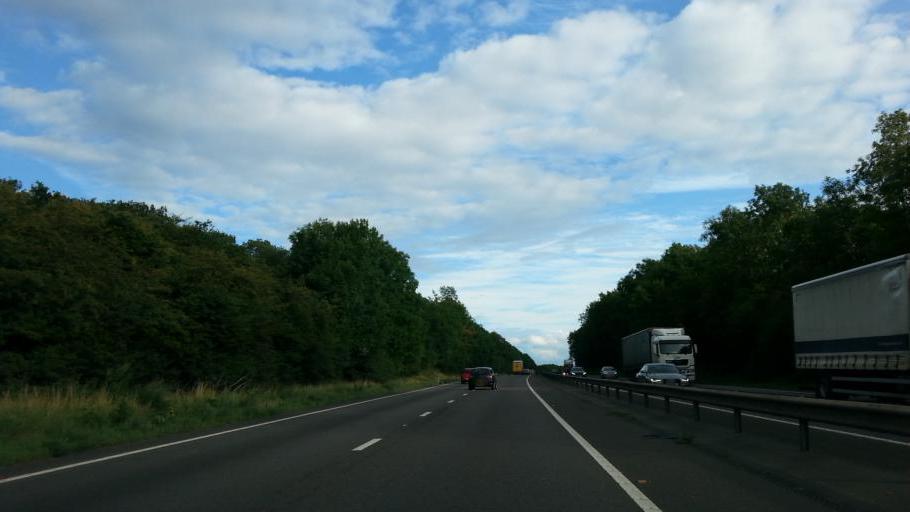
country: GB
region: England
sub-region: Nottinghamshire
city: Newark on Trent
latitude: 53.0839
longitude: -0.7756
